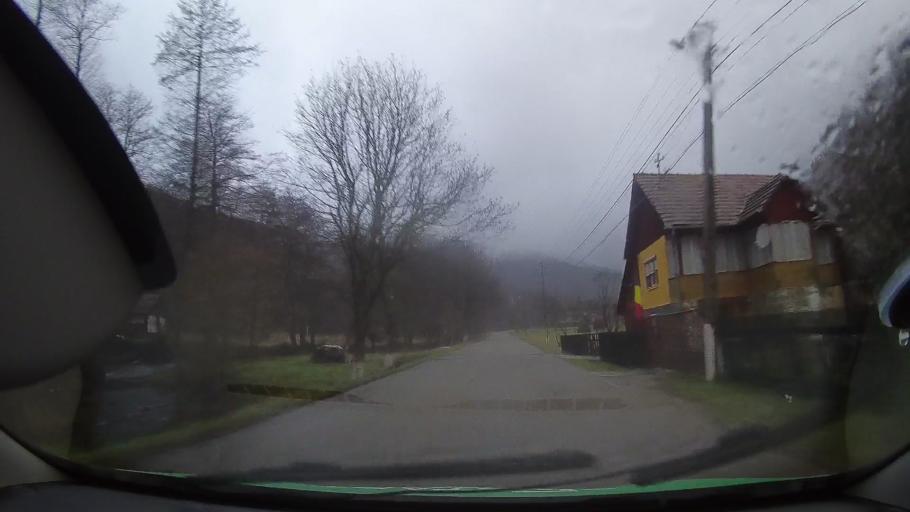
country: RO
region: Hunedoara
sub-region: Comuna Ribita
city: Ribita
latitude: 46.2544
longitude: 22.7488
